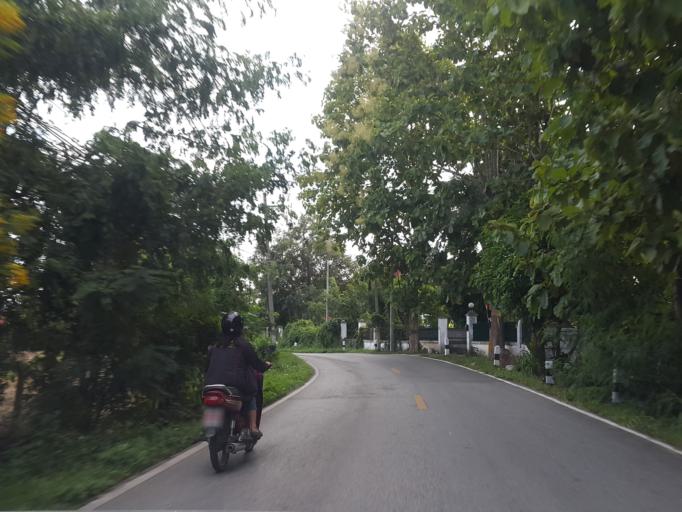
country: TH
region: Chiang Mai
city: San Sai
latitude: 18.8712
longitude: 99.0945
